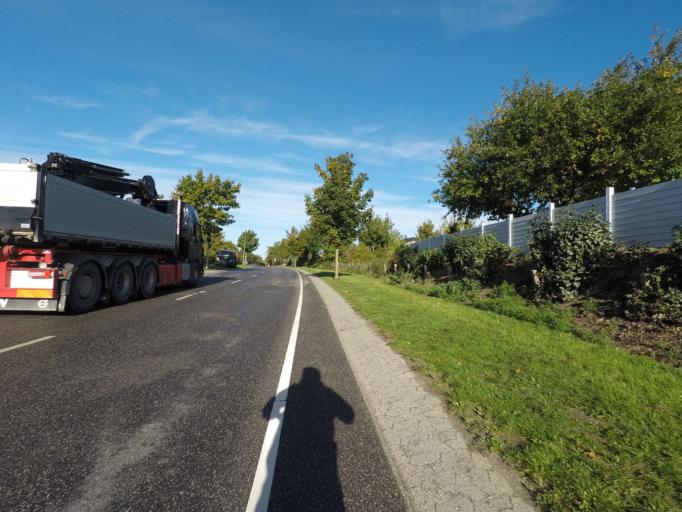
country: DK
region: Capital Region
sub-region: Egedal Kommune
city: Smorumnedre
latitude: 55.7426
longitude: 12.2984
